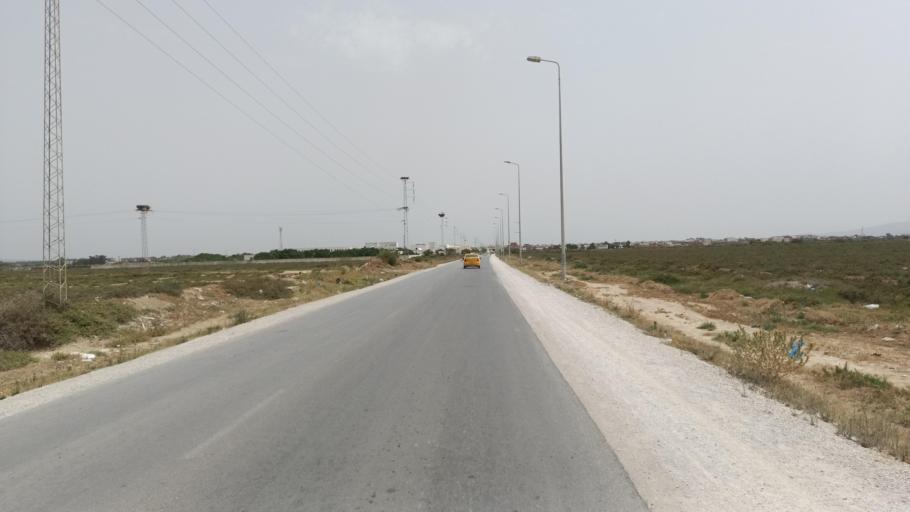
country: TN
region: Nabul
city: Manzil Bu Zalafah
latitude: 36.7161
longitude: 10.4781
